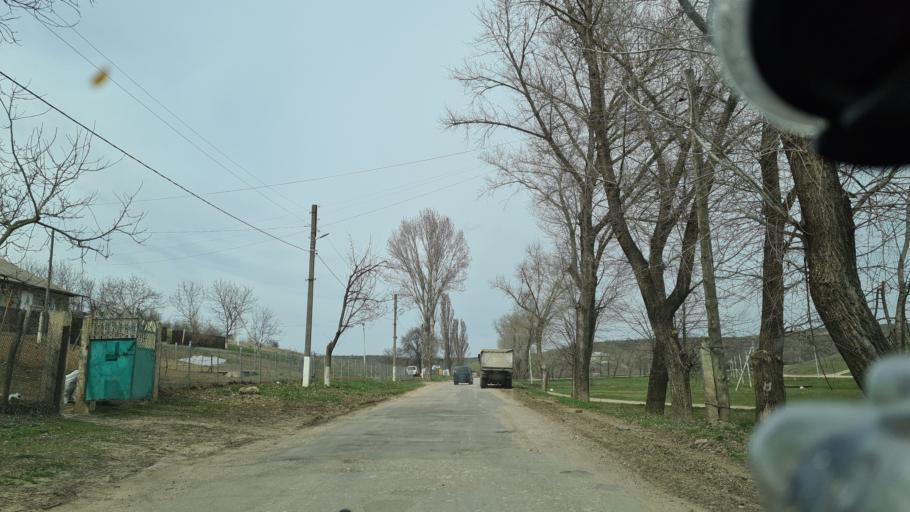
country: MD
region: Chisinau
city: Singera
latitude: 46.8386
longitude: 28.9794
